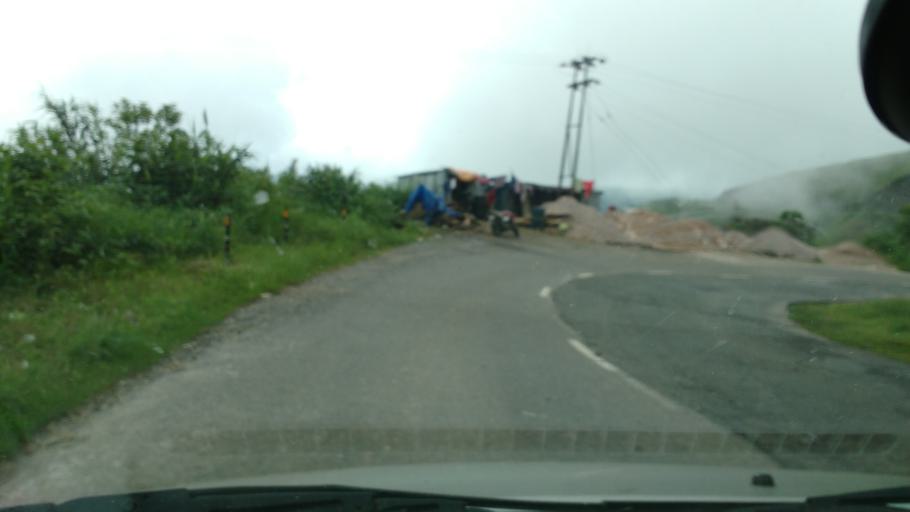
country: IN
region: Meghalaya
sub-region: East Khasi Hills
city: Cherrapunji
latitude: 25.3737
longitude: 91.8768
